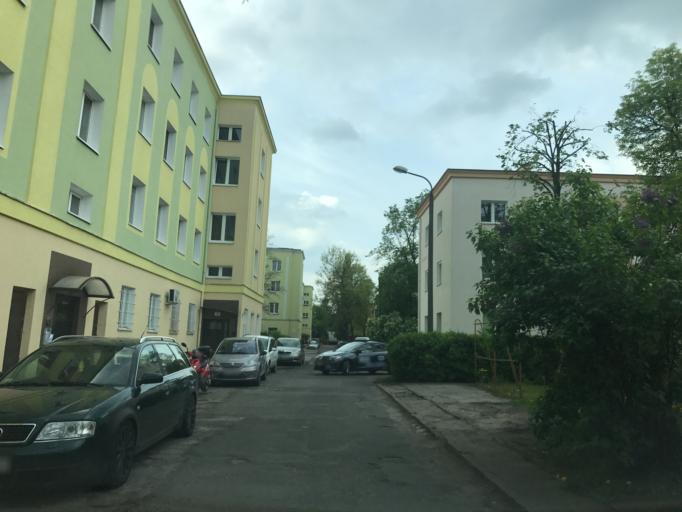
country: PL
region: Kujawsko-Pomorskie
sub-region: Bydgoszcz
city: Bydgoszcz
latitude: 53.1418
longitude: 18.0271
